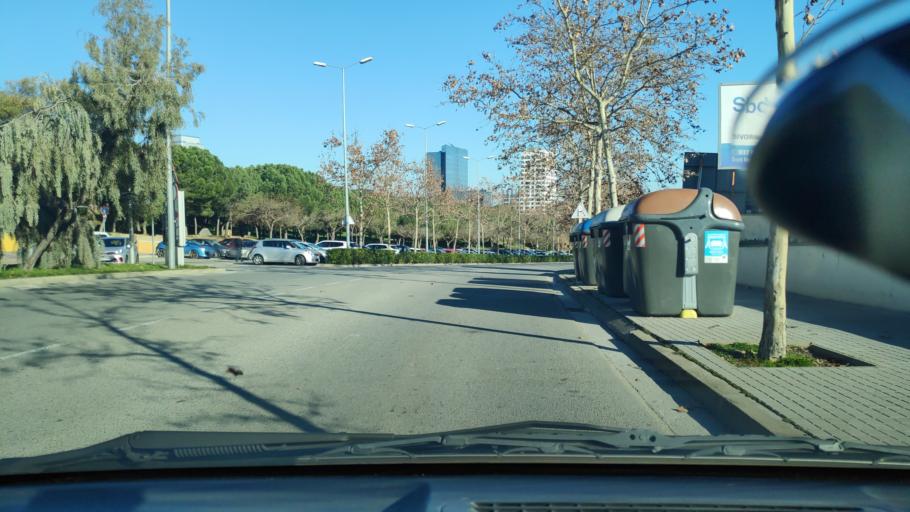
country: ES
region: Catalonia
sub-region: Provincia de Barcelona
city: Sabadell
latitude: 41.5505
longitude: 2.0931
